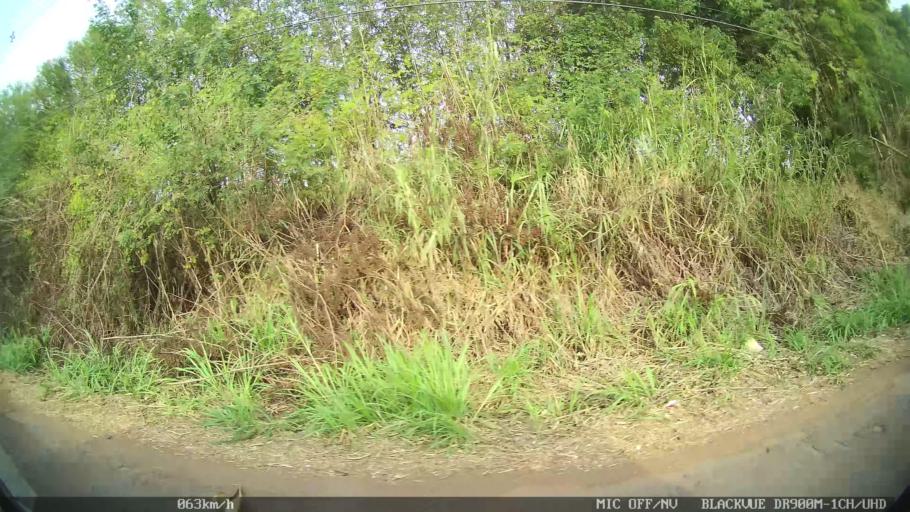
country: BR
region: Sao Paulo
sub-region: Piracicaba
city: Piracicaba
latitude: -22.6962
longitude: -47.5865
